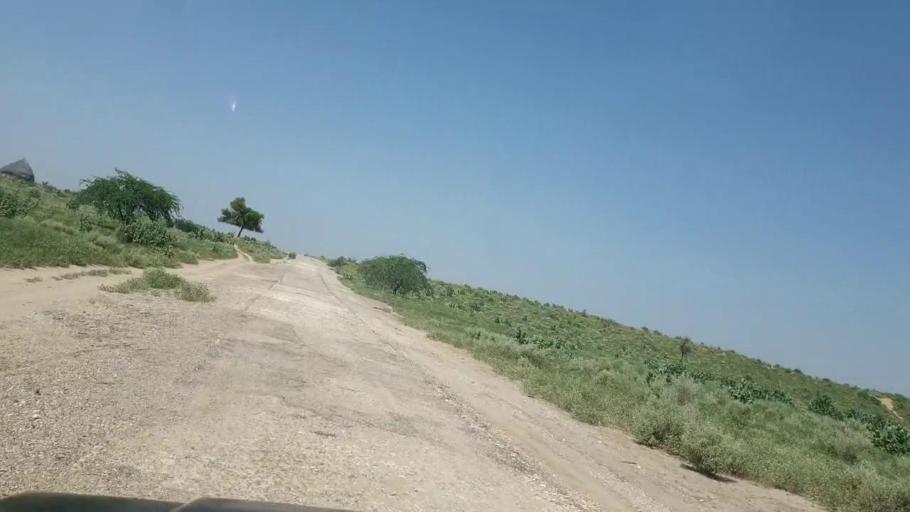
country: PK
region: Sindh
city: Chor
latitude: 25.3576
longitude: 70.3317
